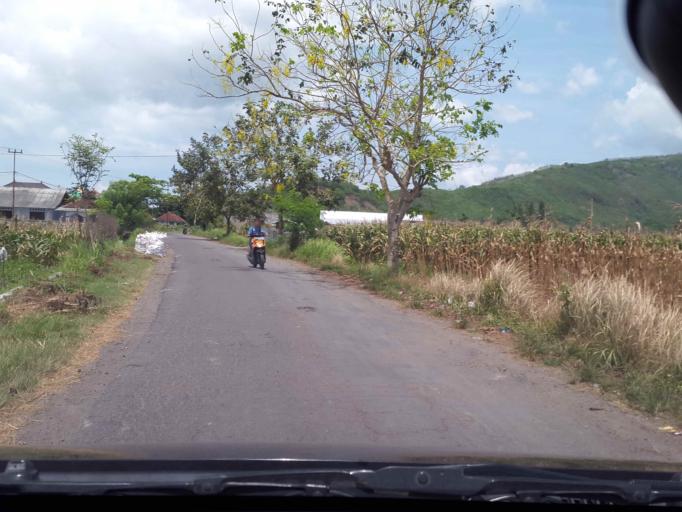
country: ID
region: West Nusa Tenggara
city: Jelateng Timur
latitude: -8.6879
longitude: 116.0989
